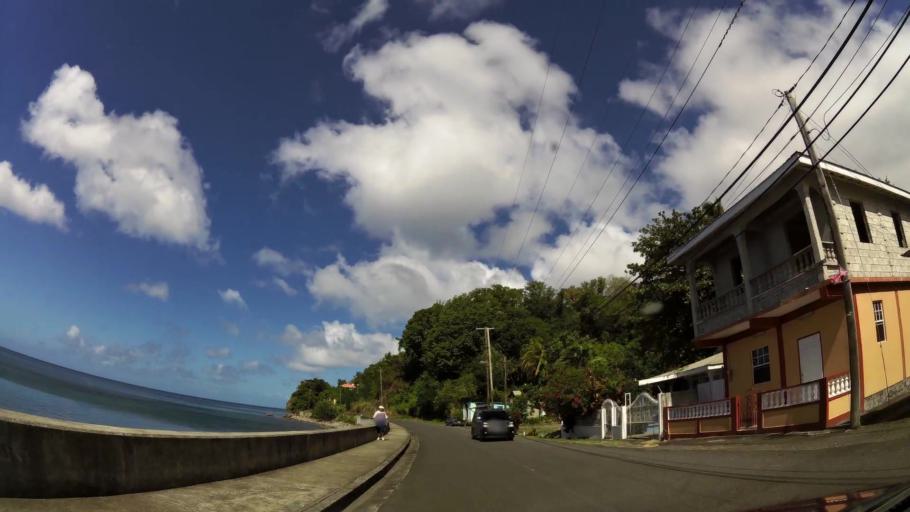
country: DM
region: Saint John
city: Portsmouth
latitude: 15.5995
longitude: -61.4615
